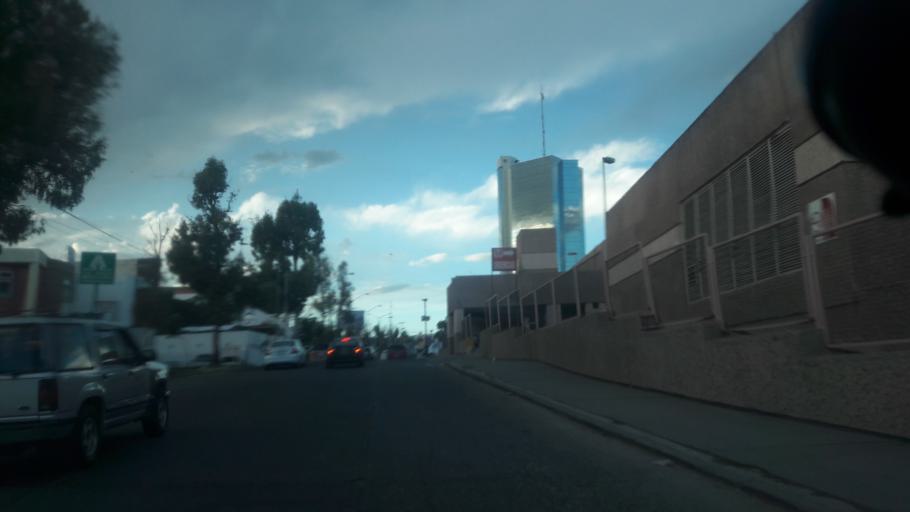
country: MX
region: Guanajuato
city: Leon
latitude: 21.1403
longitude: -101.6892
